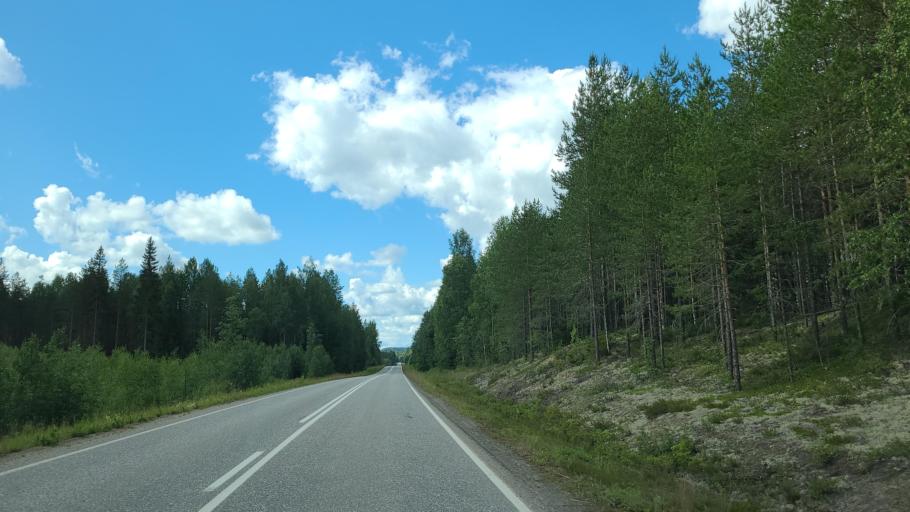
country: FI
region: Northern Savo
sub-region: Koillis-Savo
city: Kaavi
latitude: 62.9843
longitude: 28.8115
